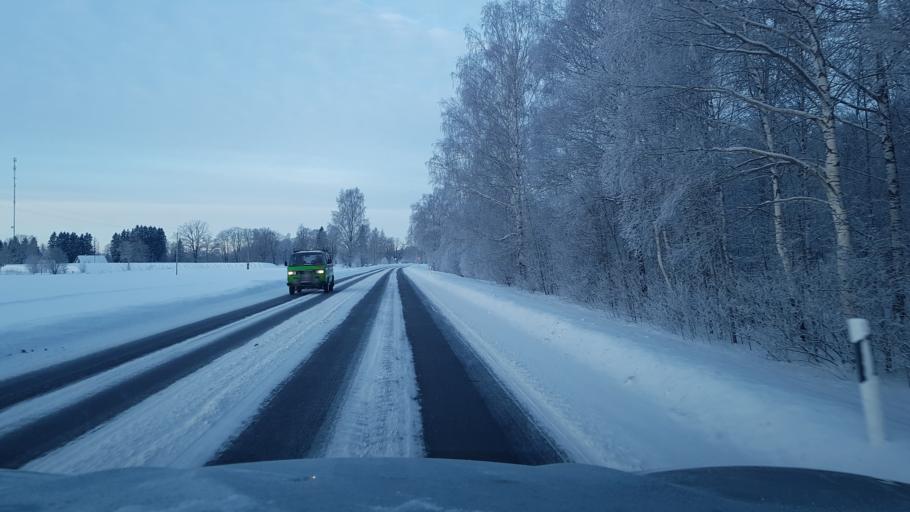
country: EE
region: Ida-Virumaa
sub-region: Johvi vald
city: Johvi
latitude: 59.3451
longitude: 27.4422
